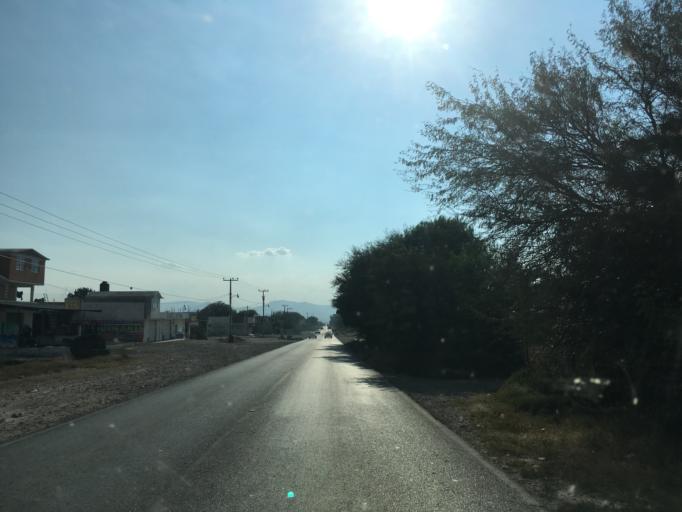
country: MX
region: Hidalgo
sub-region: Ixmiquilpan
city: El Nith
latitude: 20.5528
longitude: -99.1626
